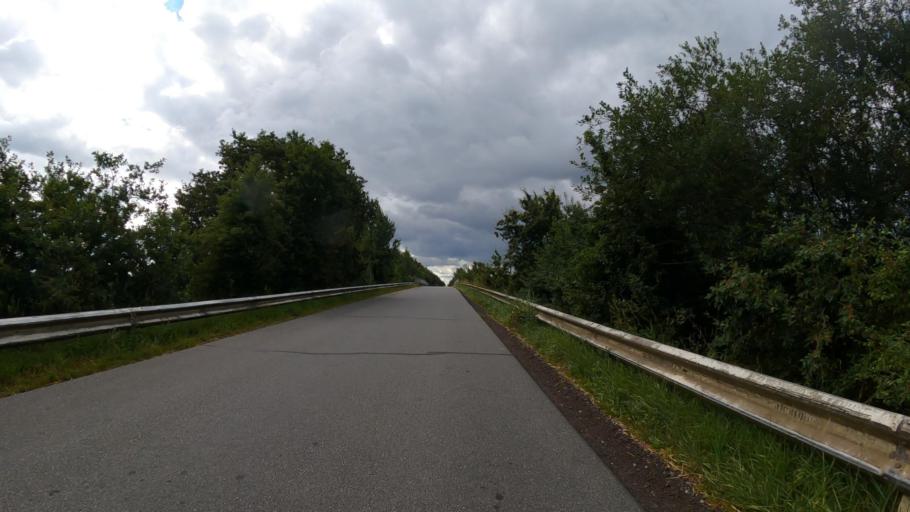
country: DE
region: Schleswig-Holstein
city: Padenstedt
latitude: 54.0389
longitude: 9.9167
